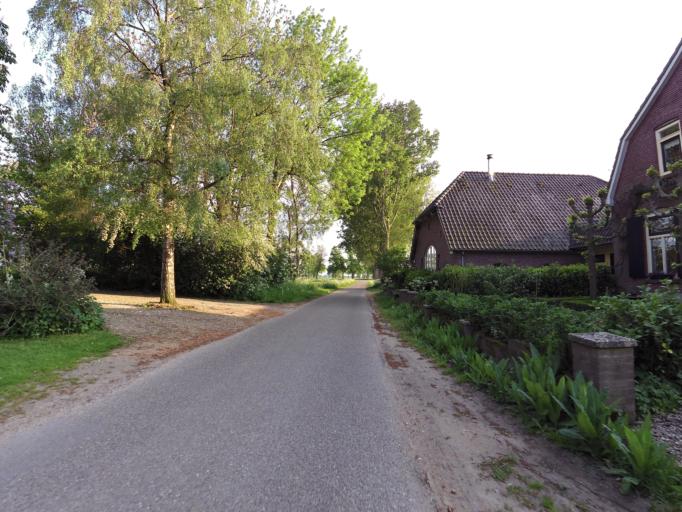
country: NL
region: Gelderland
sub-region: Oude IJsselstreek
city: Gendringen
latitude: 51.8618
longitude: 6.3572
